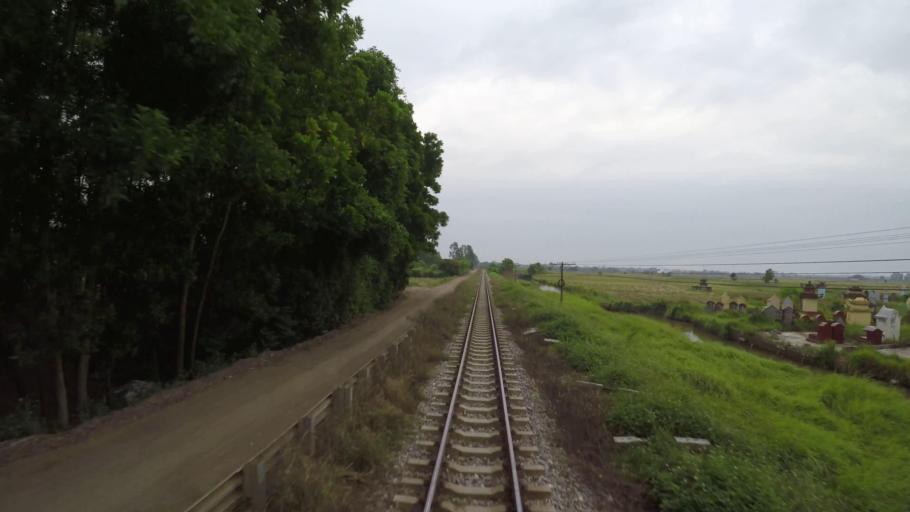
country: VN
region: Hai Duong
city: Ke Sat
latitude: 20.9658
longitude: 106.1325
